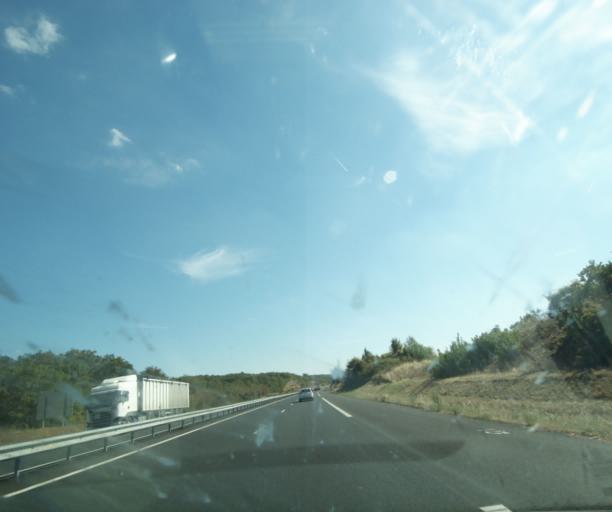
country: FR
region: Limousin
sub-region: Departement de la Correze
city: Brive-la-Gaillarde
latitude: 45.0448
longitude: 1.5187
